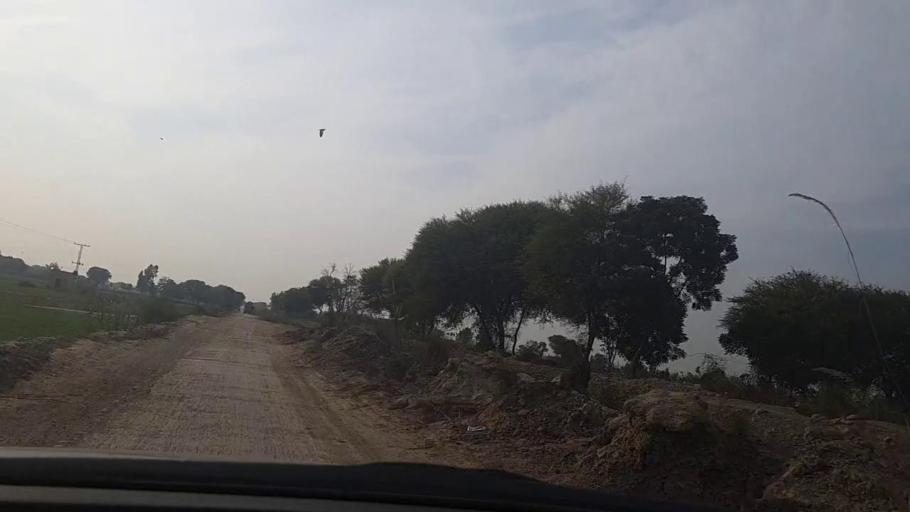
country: PK
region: Sindh
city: Daulatpur
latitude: 26.3340
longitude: 68.0676
